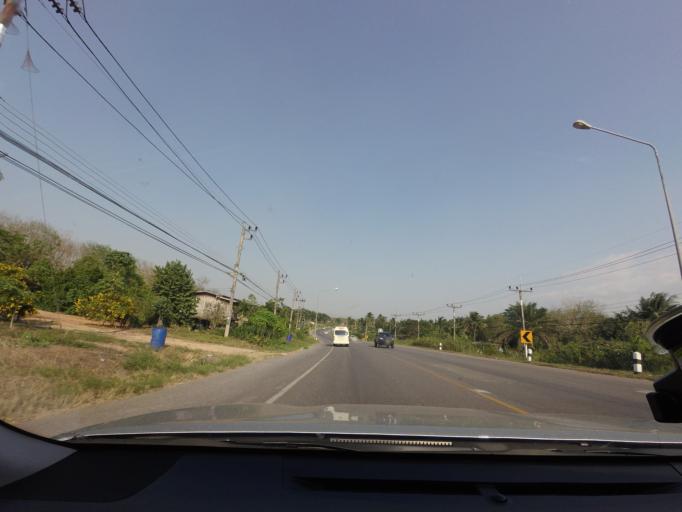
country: TH
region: Surat Thani
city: Phrasaeng
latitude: 8.5735
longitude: 99.2169
